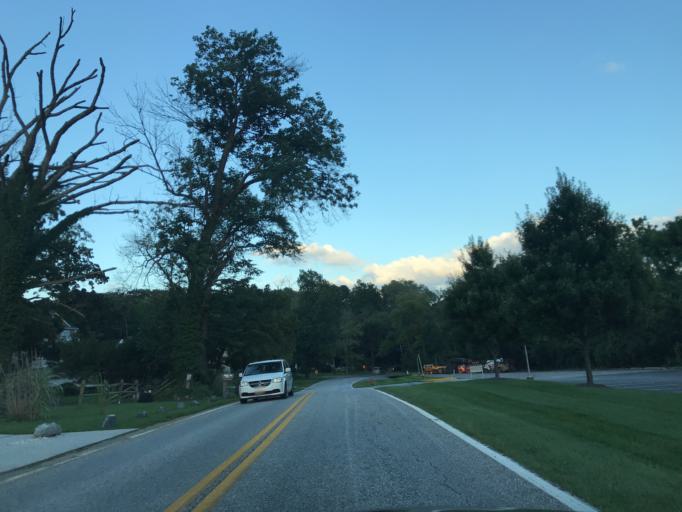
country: US
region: Maryland
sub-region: Baltimore County
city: Woodlawn
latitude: 39.3160
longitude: -76.7272
